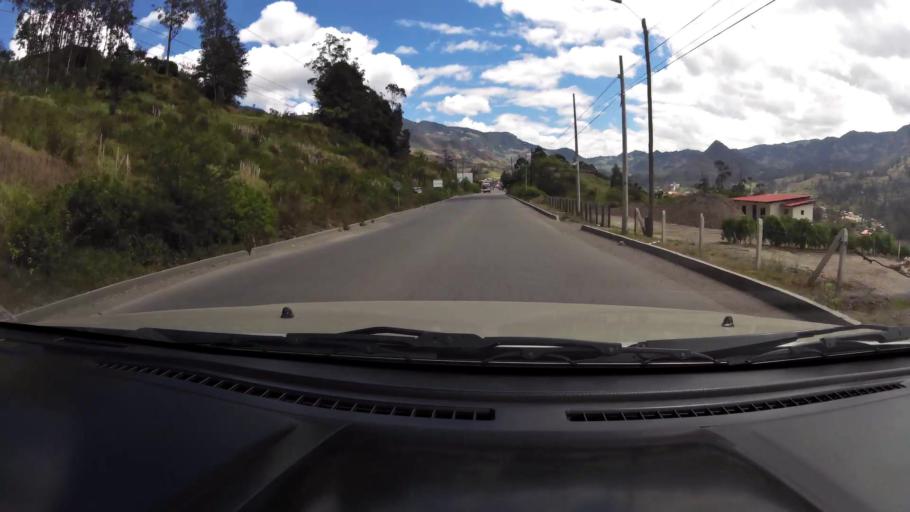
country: EC
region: Azuay
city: Cuenca
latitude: -3.1657
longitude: -79.1534
